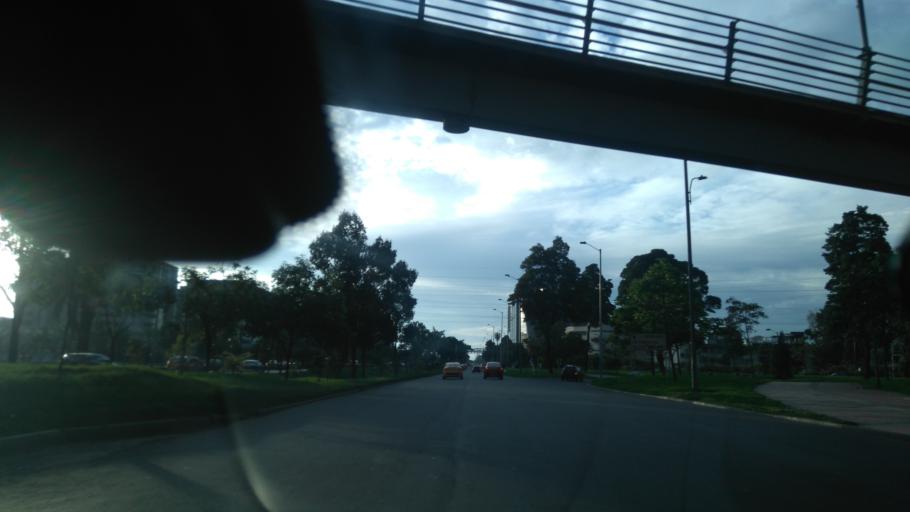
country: CO
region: Bogota D.C.
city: Bogota
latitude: 4.6540
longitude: -74.1033
